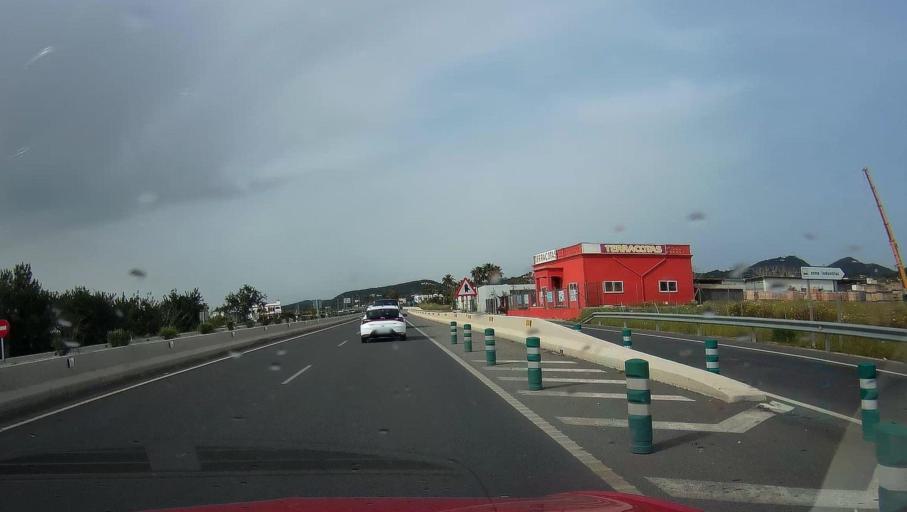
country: ES
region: Balearic Islands
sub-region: Illes Balears
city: Ibiza
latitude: 38.9314
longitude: 1.4435
